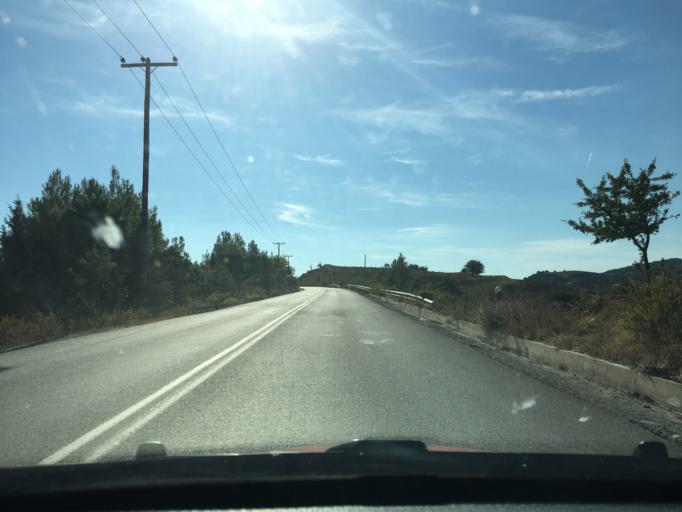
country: GR
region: Central Macedonia
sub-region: Nomos Chalkidikis
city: Ierissos
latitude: 40.3823
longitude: 23.8569
